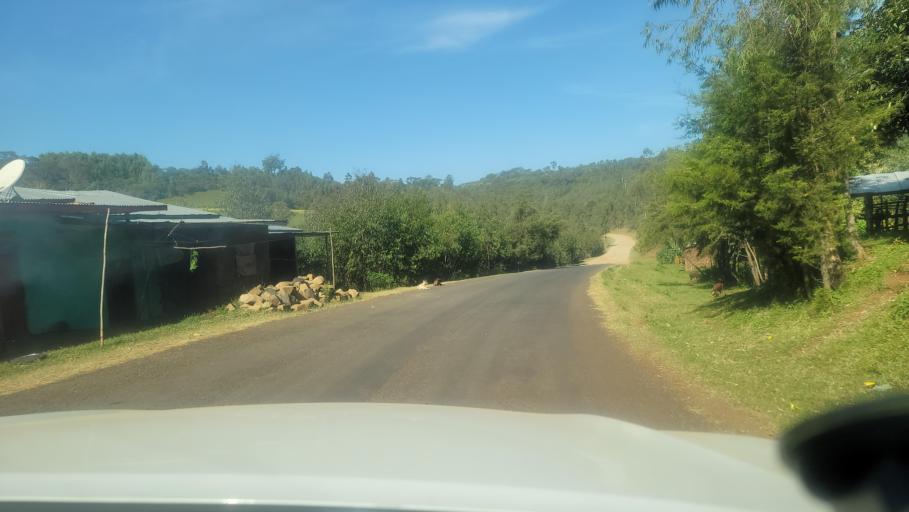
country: ET
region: Oromiya
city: Agaro
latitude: 7.7994
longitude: 36.4727
